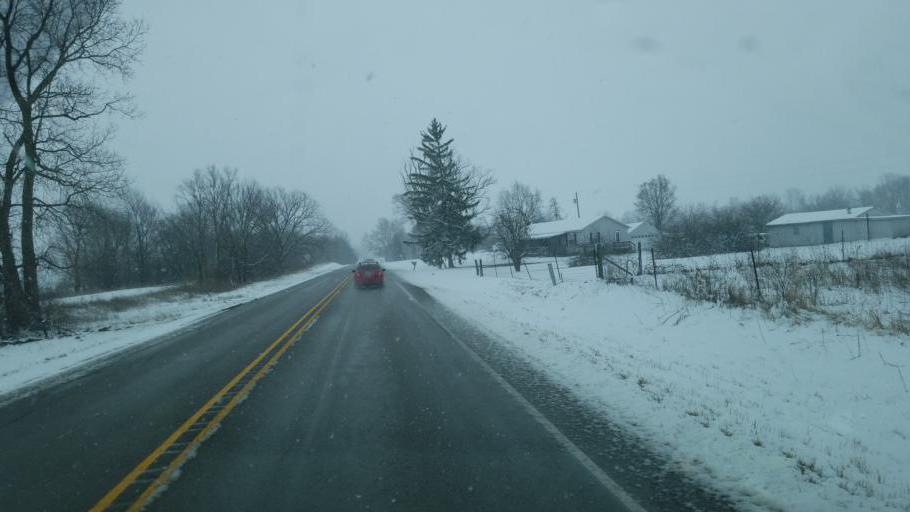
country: US
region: Indiana
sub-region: Randolph County
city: Parker City
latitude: 40.0518
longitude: -85.2240
